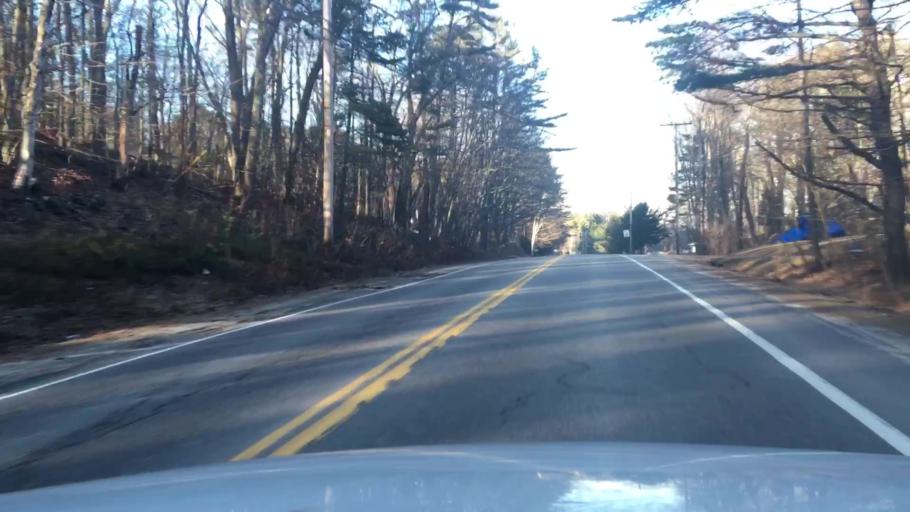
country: US
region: Maine
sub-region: Cumberland County
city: Brunswick
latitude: 43.8513
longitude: -69.9129
